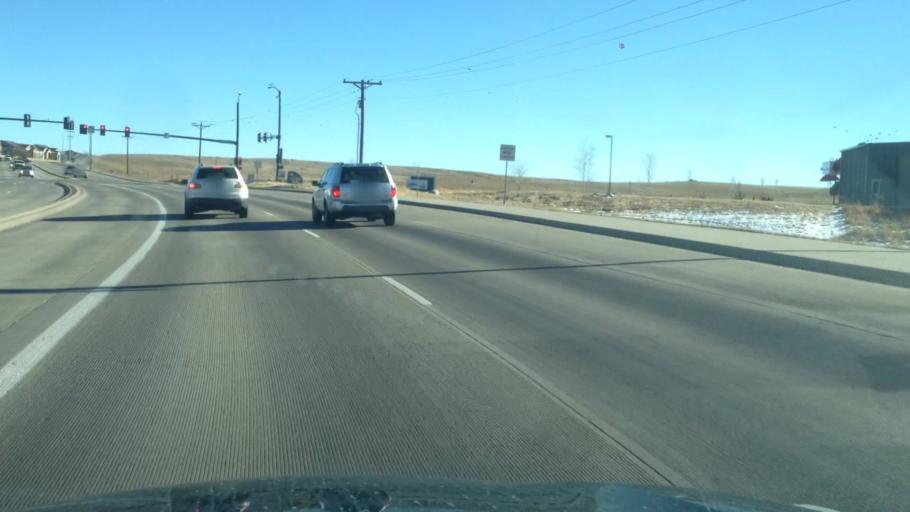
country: US
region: Colorado
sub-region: Arapahoe County
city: Dove Valley
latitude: 39.5826
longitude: -104.8138
